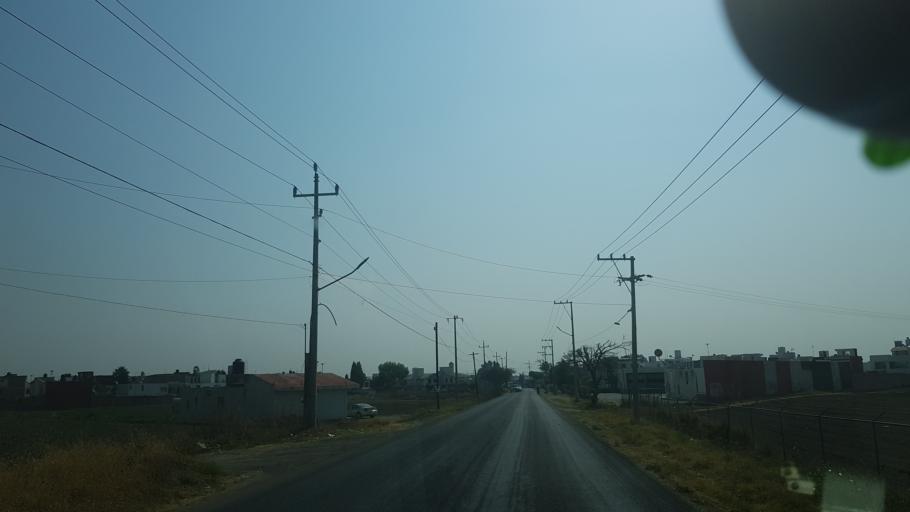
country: MX
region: Puebla
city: Cholula
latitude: 19.0552
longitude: -98.3303
